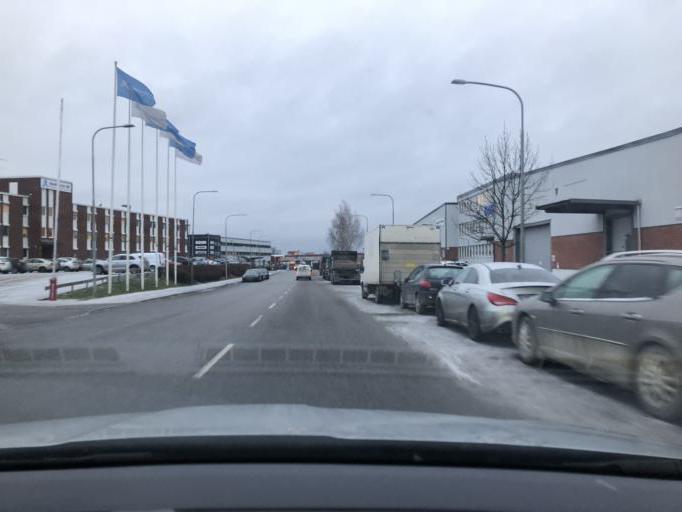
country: SE
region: Stockholm
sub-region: Jarfalla Kommun
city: Jakobsberg
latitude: 59.3901
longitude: 17.8761
